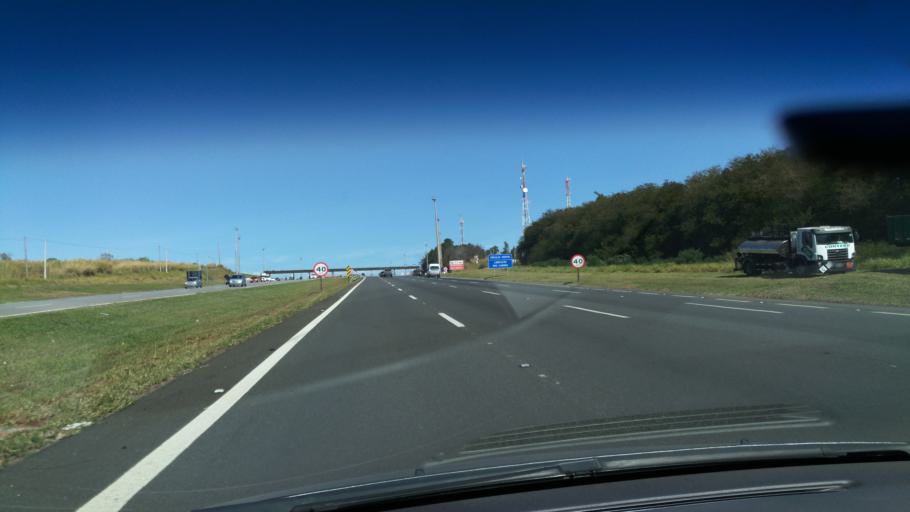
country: BR
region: Sao Paulo
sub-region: Jaguariuna
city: Jaguariuna
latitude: -22.7666
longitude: -47.0218
